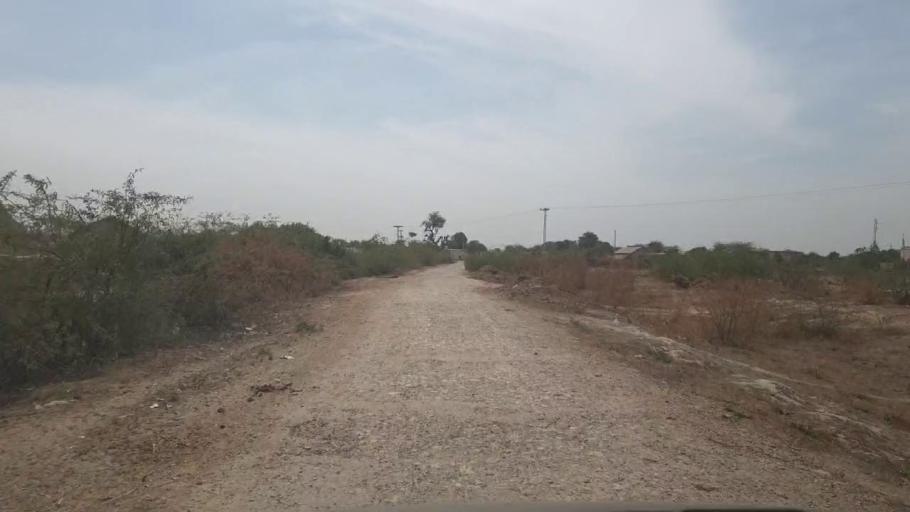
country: PK
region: Sindh
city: Kunri
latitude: 25.2268
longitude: 69.6846
